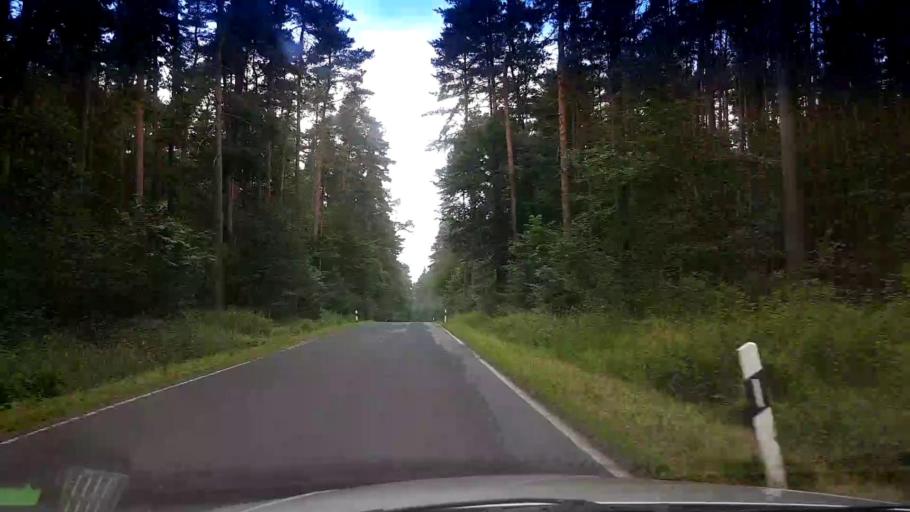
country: DE
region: Bavaria
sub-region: Upper Franconia
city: Oberhaid
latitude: 49.9455
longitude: 10.8159
